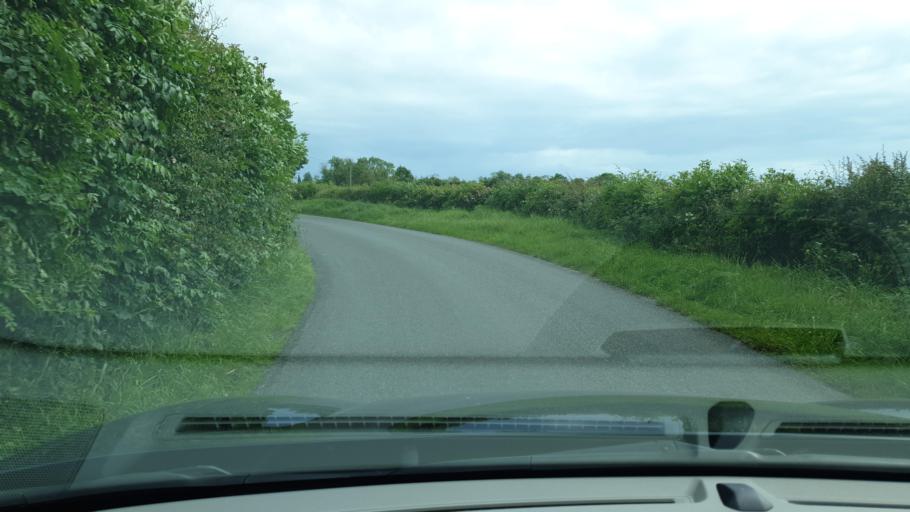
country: IE
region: Leinster
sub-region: An Mhi
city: Ratoath
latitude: 53.4620
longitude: -6.4674
